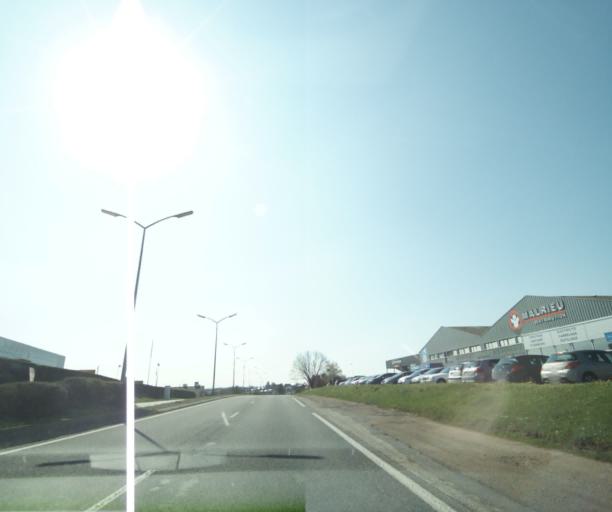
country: FR
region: Midi-Pyrenees
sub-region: Departement de l'Aveyron
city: Olemps
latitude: 44.3702
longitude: 2.5481
